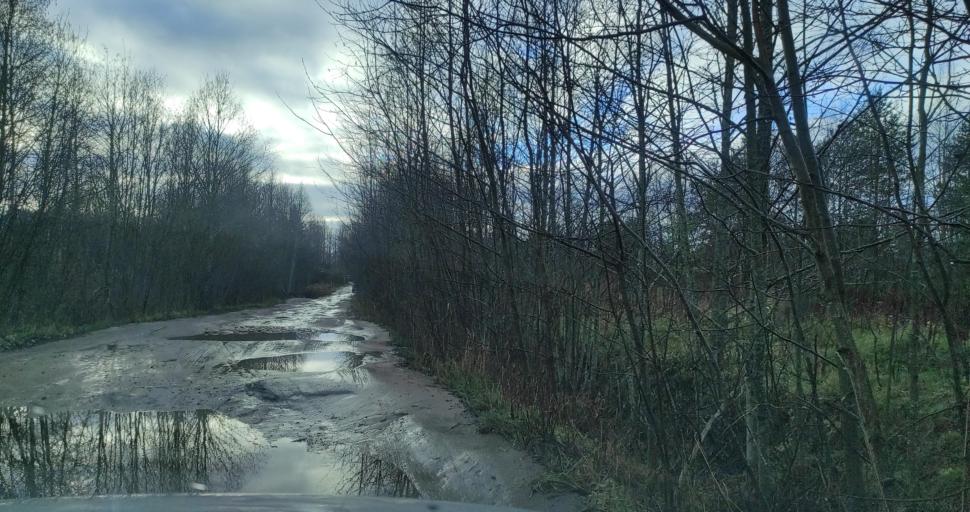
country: RU
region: Republic of Karelia
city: Pitkyaranta
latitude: 61.7350
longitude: 31.3865
